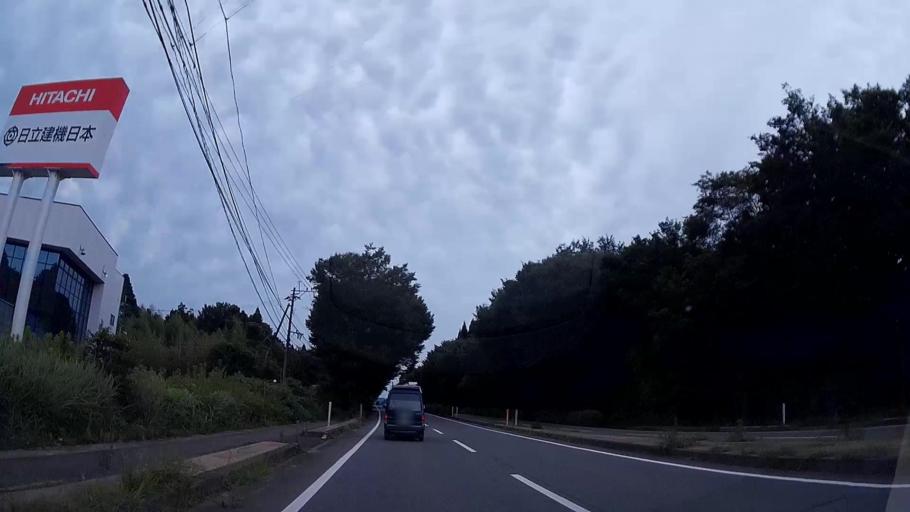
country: JP
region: Kumamoto
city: Ozu
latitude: 32.8945
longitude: 130.8540
